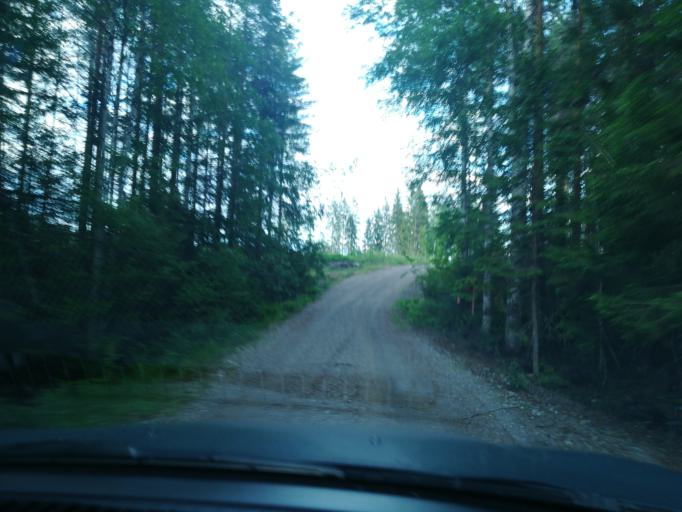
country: FI
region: Southern Savonia
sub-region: Mikkeli
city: Puumala
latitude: 61.6143
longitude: 28.1536
